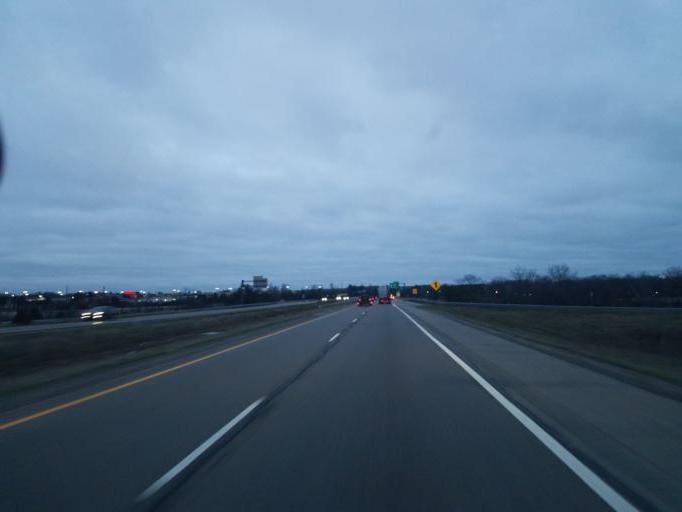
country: US
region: Michigan
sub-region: Washtenaw County
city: Ann Arbor
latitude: 42.2523
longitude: -83.6836
